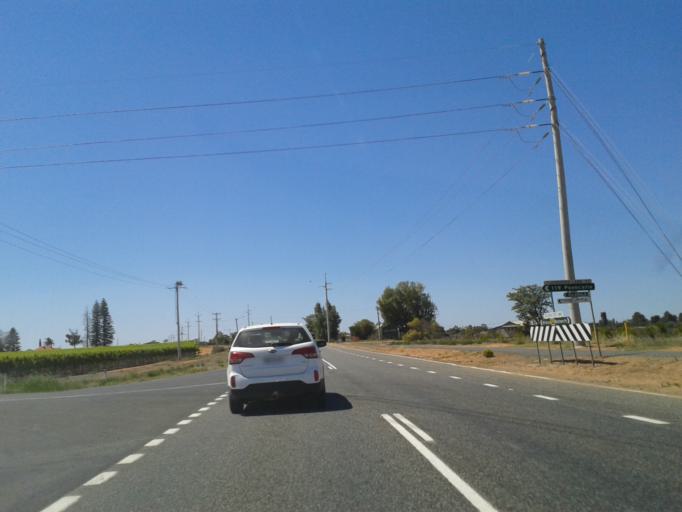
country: AU
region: New South Wales
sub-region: Wentworth
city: Dareton
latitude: -34.0940
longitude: 142.0495
